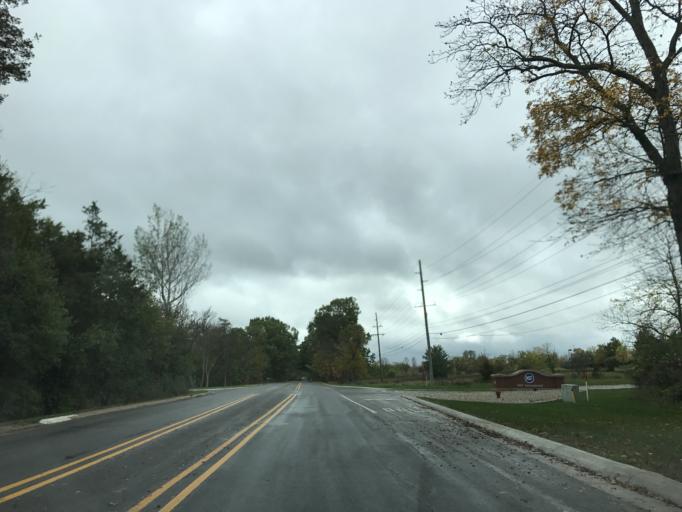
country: US
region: Michigan
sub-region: Washtenaw County
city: Ann Arbor
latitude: 42.2848
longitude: -83.6715
